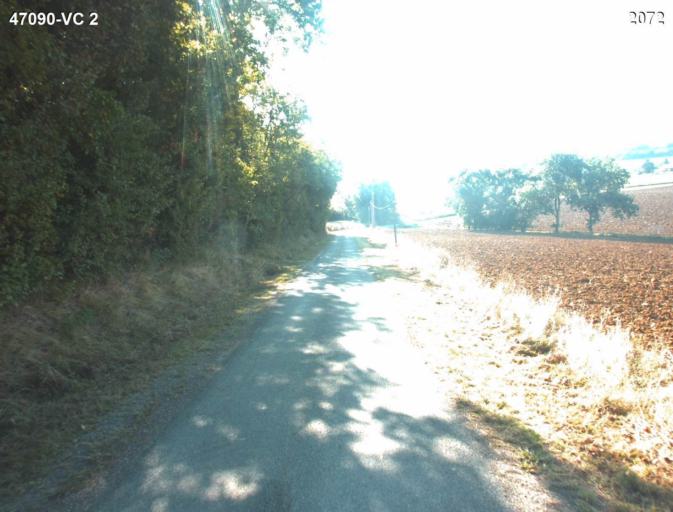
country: FR
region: Aquitaine
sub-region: Departement du Lot-et-Garonne
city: Nerac
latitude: 44.1764
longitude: 0.3762
